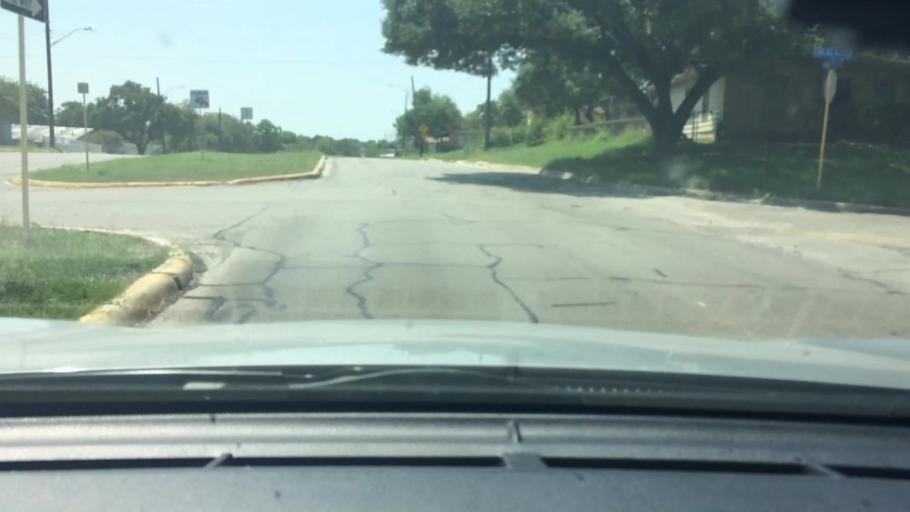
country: US
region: Texas
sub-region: Bexar County
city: San Antonio
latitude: 29.3726
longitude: -98.4355
